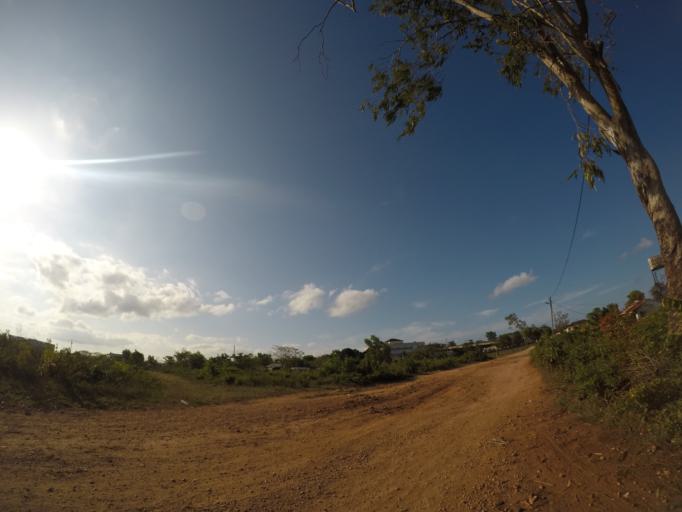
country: TZ
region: Zanzibar Central/South
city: Koani
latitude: -6.2012
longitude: 39.3085
